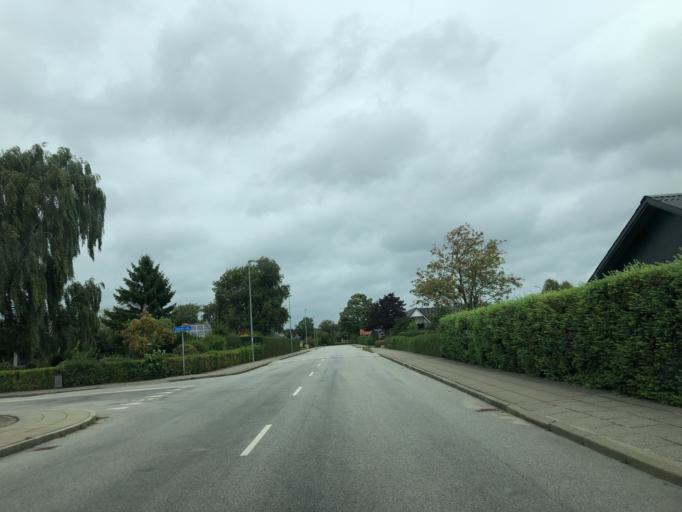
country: DK
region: Central Jutland
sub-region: Herning Kommune
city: Snejbjerg
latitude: 56.1291
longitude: 8.8985
